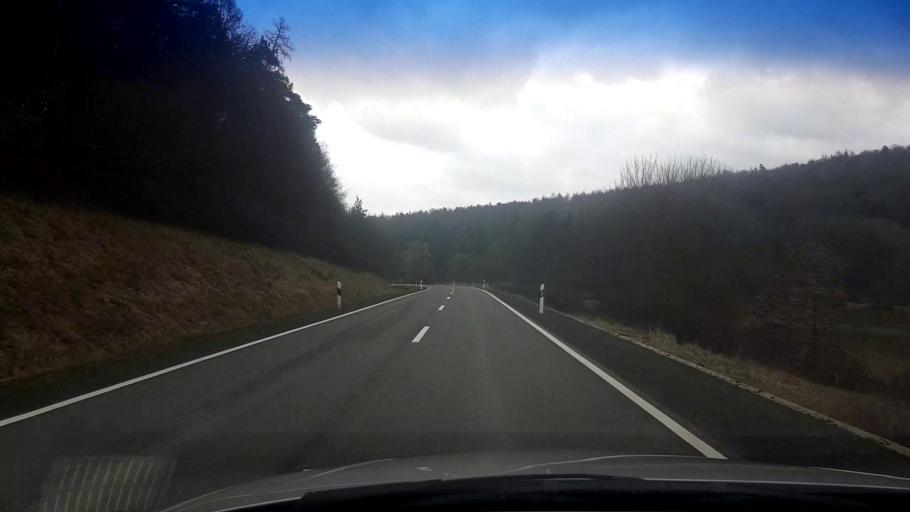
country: DE
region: Bavaria
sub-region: Regierungsbezirk Unterfranken
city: Eltmann
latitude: 49.9366
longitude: 10.6265
